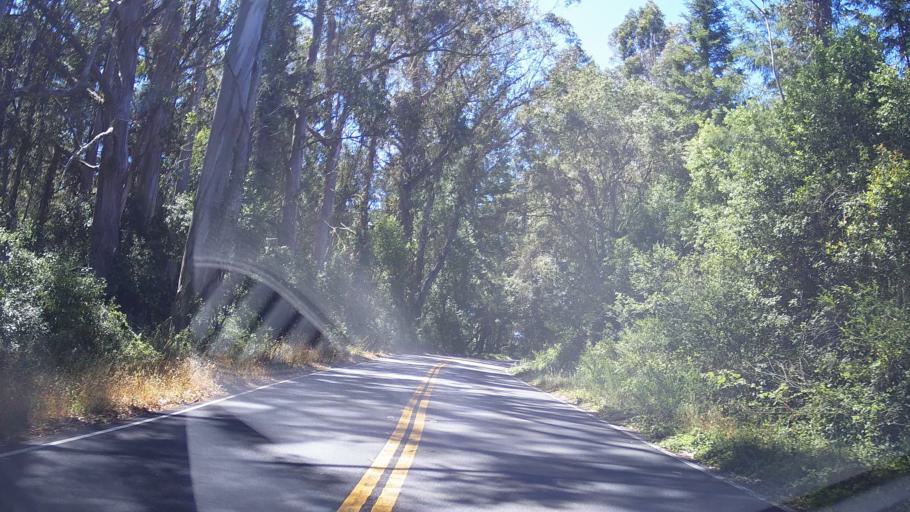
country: US
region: California
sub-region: Marin County
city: Bolinas
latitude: 37.9619
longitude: -122.7211
